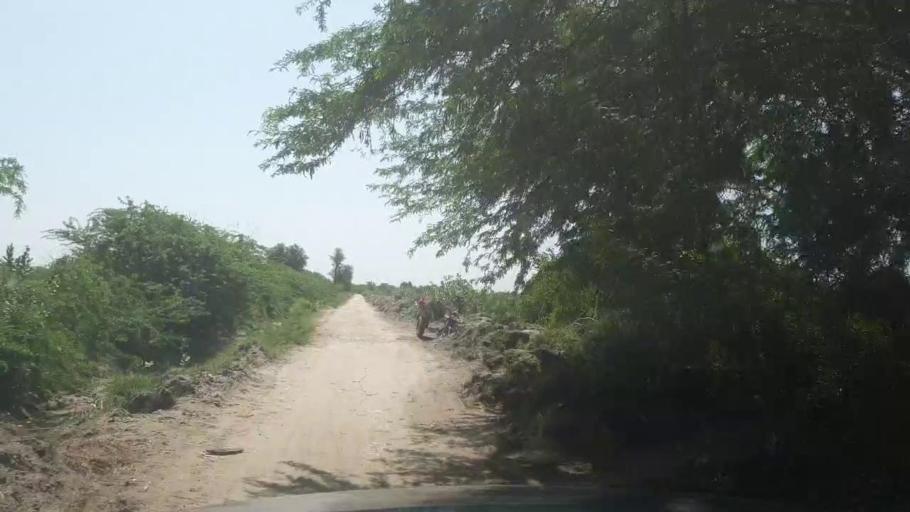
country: PK
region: Sindh
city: Khairpur
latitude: 27.3589
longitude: 69.0357
